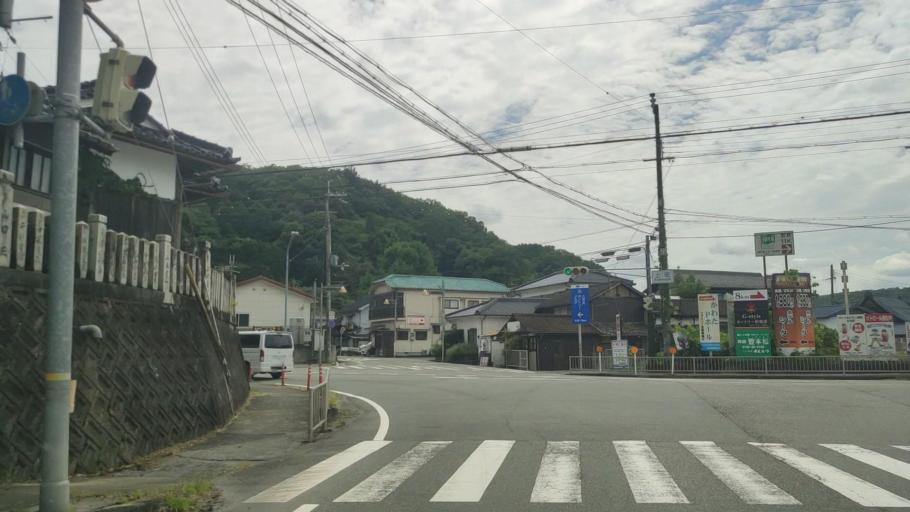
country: JP
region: Hyogo
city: Yamazakicho-nakabirose
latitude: 35.0068
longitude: 134.3635
